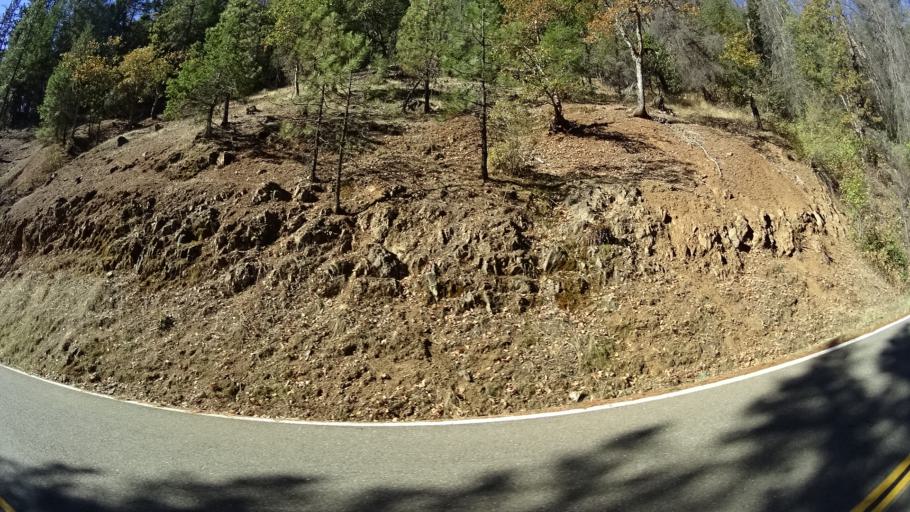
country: US
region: California
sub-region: Trinity County
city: Weaverville
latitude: 41.1830
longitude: -123.0809
